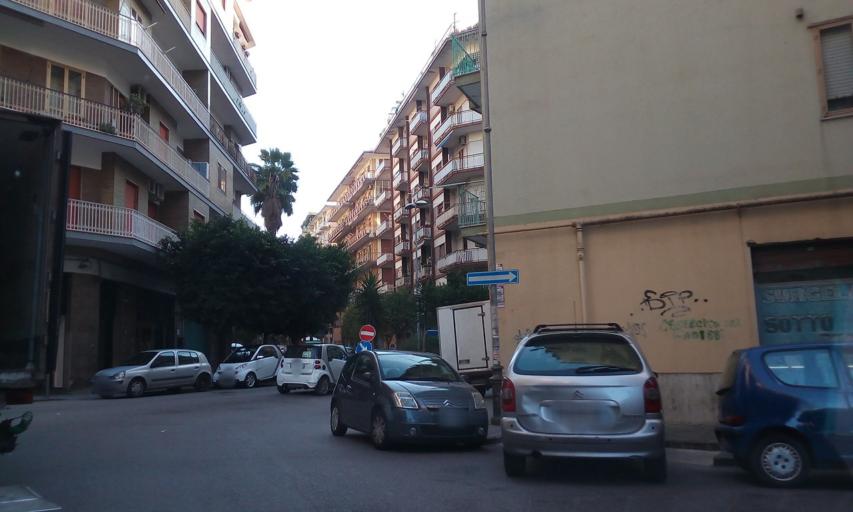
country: IT
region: Campania
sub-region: Provincia di Salerno
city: Salerno
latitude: 40.6790
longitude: 14.7766
